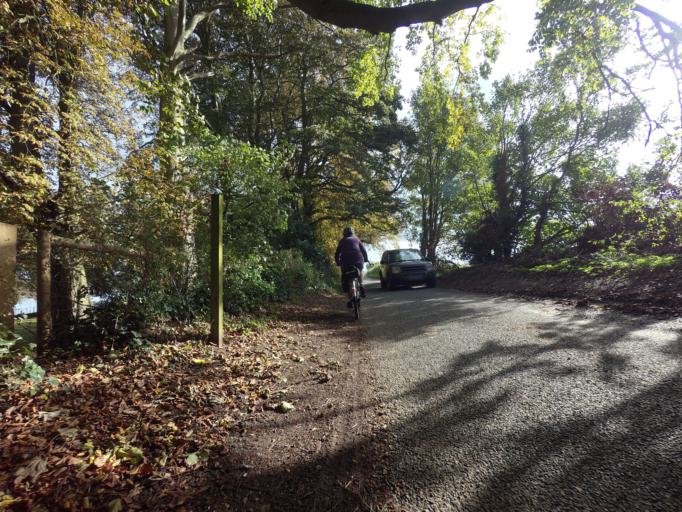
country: GB
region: England
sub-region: Norfolk
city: Snettisham
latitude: 52.8635
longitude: 0.5104
